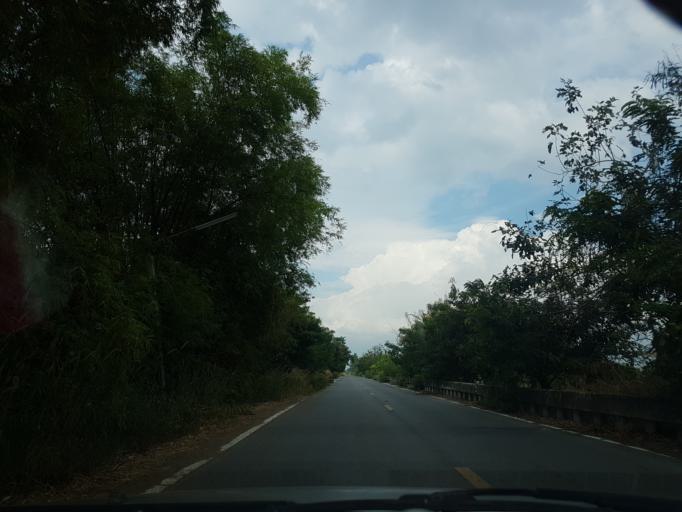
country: TH
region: Sara Buri
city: Nong Khae
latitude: 14.2556
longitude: 100.8913
